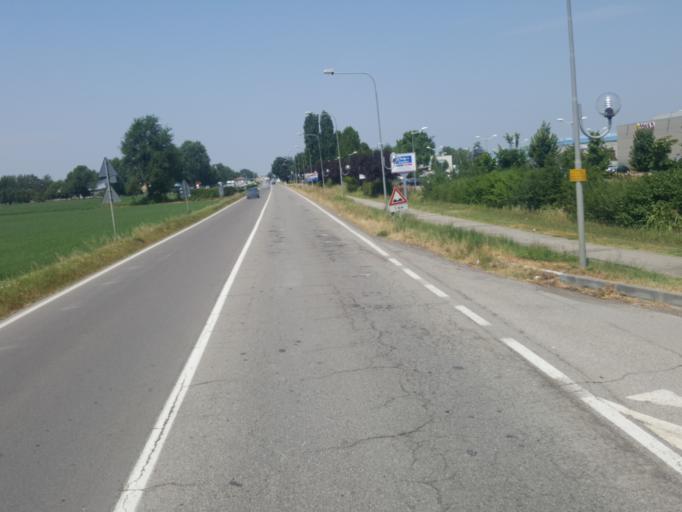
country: IT
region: Emilia-Romagna
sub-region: Provincia di Bologna
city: Calcara
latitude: 44.5640
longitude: 11.1411
